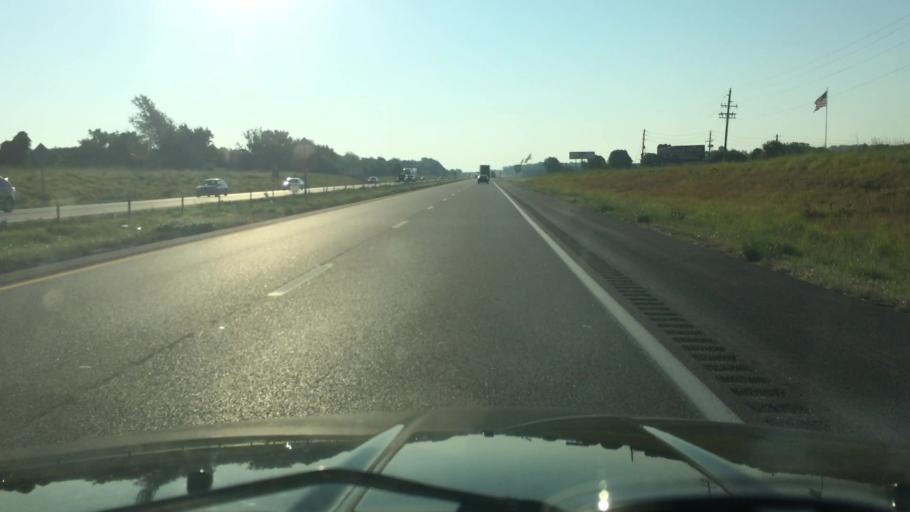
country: US
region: Missouri
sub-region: Greene County
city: Strafford
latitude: 37.2501
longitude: -93.2084
